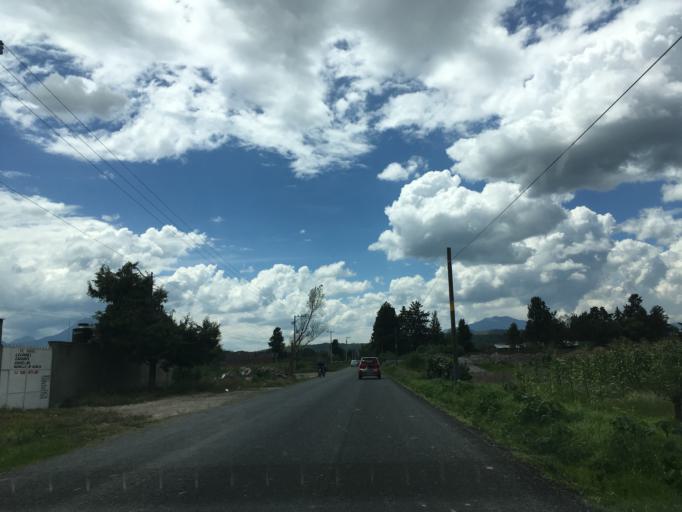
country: MX
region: Michoacan
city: Zacapu
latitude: 19.8400
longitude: -101.7535
